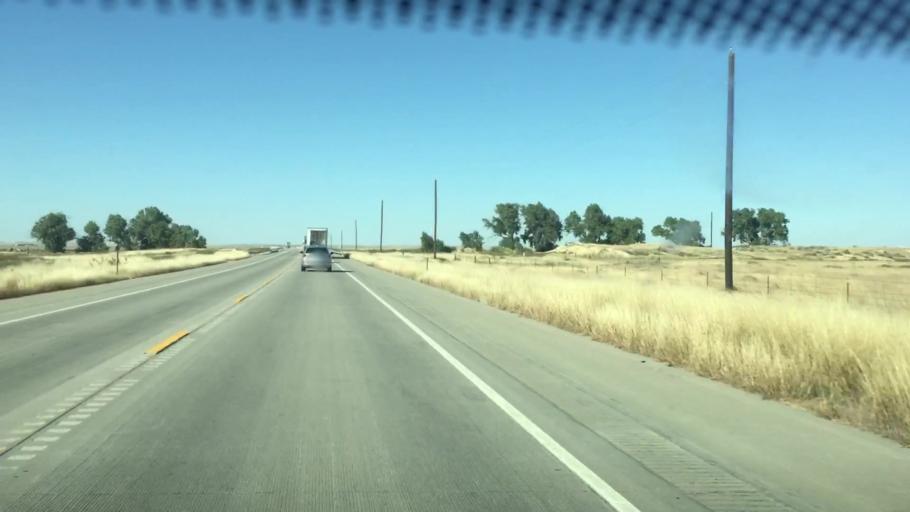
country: US
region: Colorado
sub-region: Kiowa County
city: Eads
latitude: 38.3310
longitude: -102.7198
